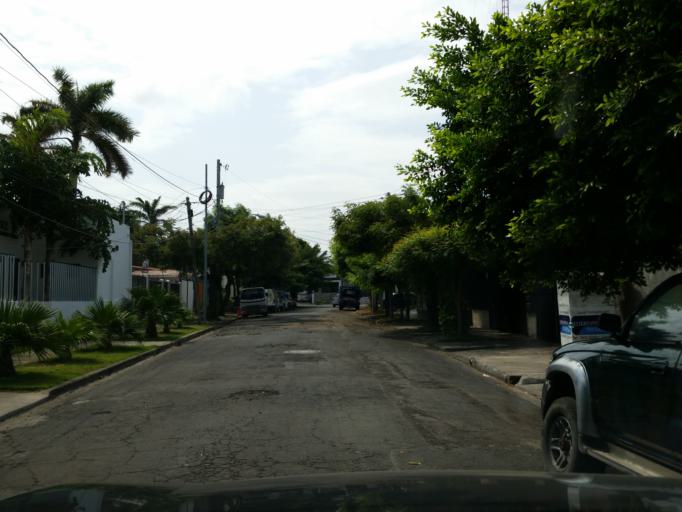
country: NI
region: Managua
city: Managua
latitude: 12.1377
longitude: -86.2789
